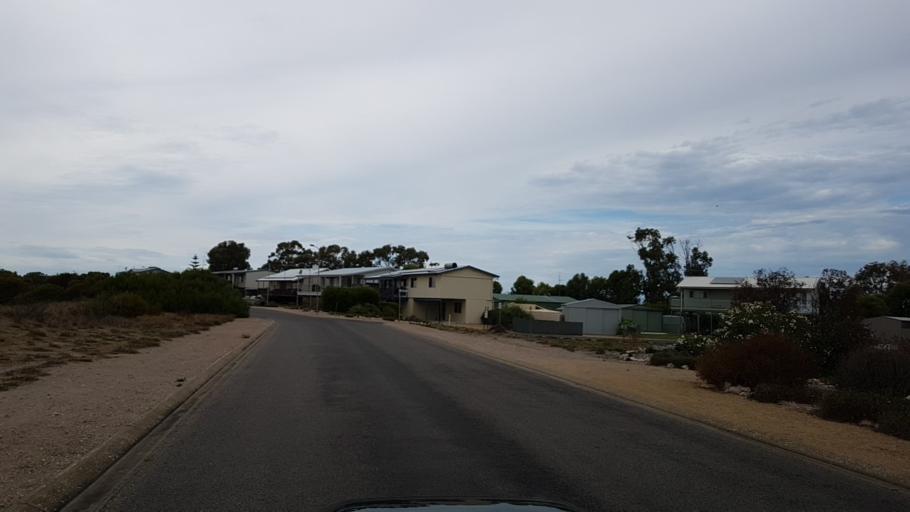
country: AU
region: South Australia
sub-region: Yorke Peninsula
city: Port Victoria
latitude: -34.9099
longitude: 137.0526
